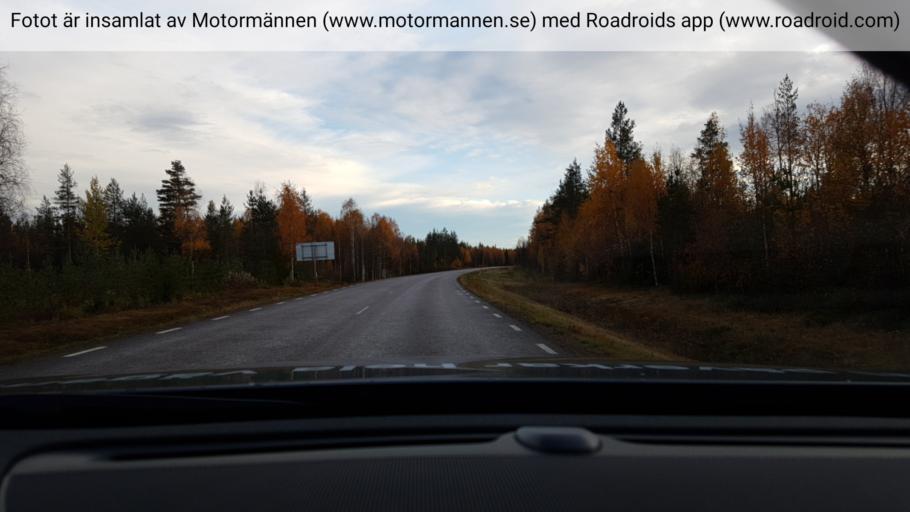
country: SE
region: Norrbotten
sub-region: Overkalix Kommun
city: OEverkalix
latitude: 66.9081
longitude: 22.7753
